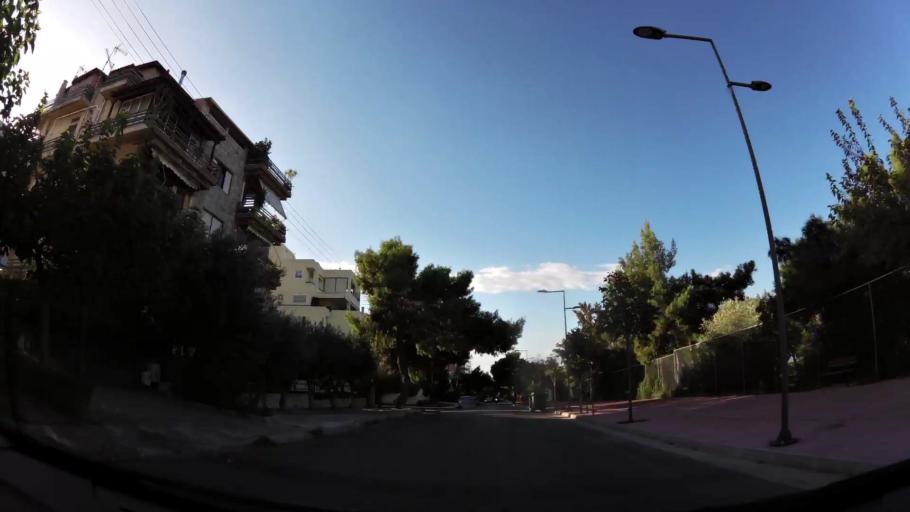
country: GR
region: Attica
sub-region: Nomarchia Athinas
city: Elliniko
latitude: 37.8782
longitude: 23.7498
